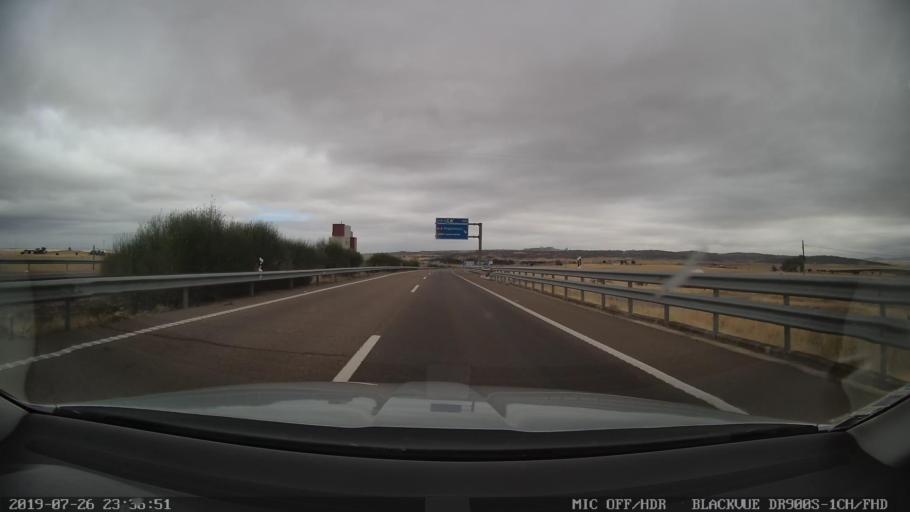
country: ES
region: Extremadura
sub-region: Provincia de Caceres
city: Trujillo
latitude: 39.4020
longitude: -5.8893
